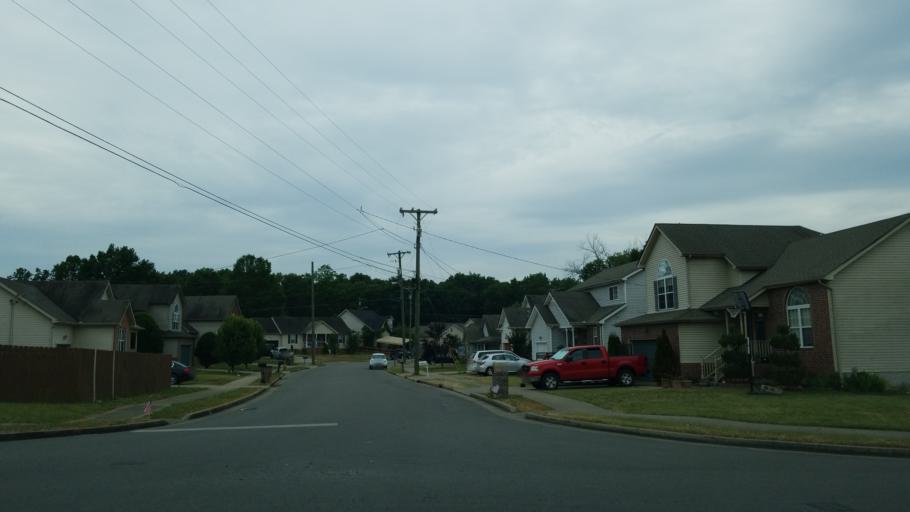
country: US
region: Tennessee
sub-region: Rutherford County
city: La Vergne
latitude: 36.0515
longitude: -86.5908
